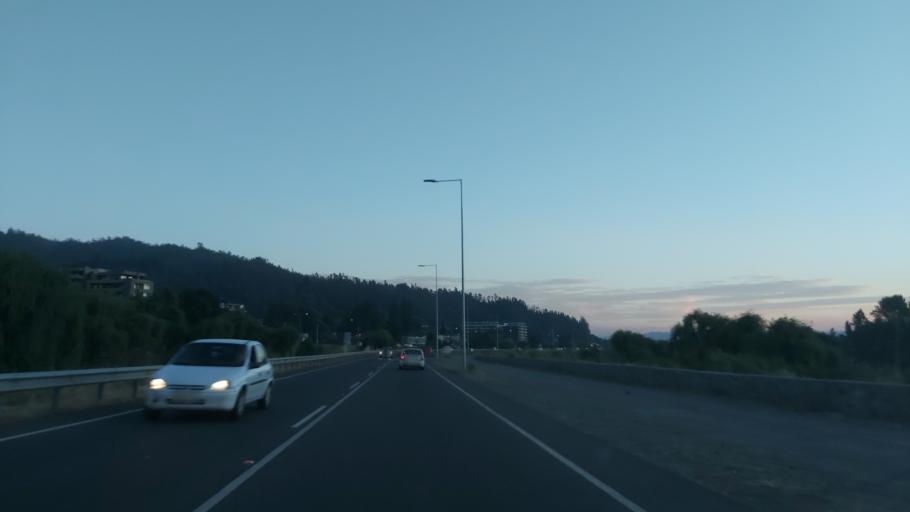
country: CL
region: Biobio
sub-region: Provincia de Concepcion
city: Chiguayante
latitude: -36.8770
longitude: -73.0400
